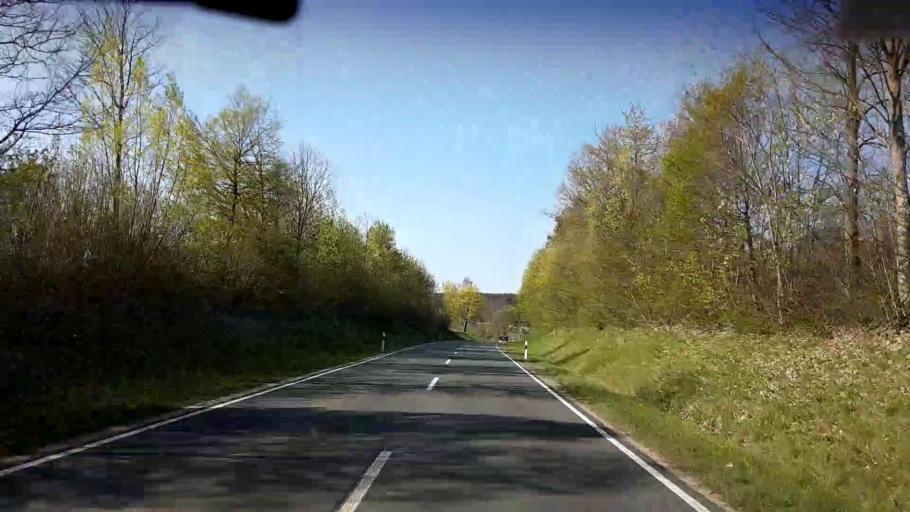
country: DE
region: Bavaria
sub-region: Upper Franconia
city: Plankenfels
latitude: 49.8942
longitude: 11.3340
